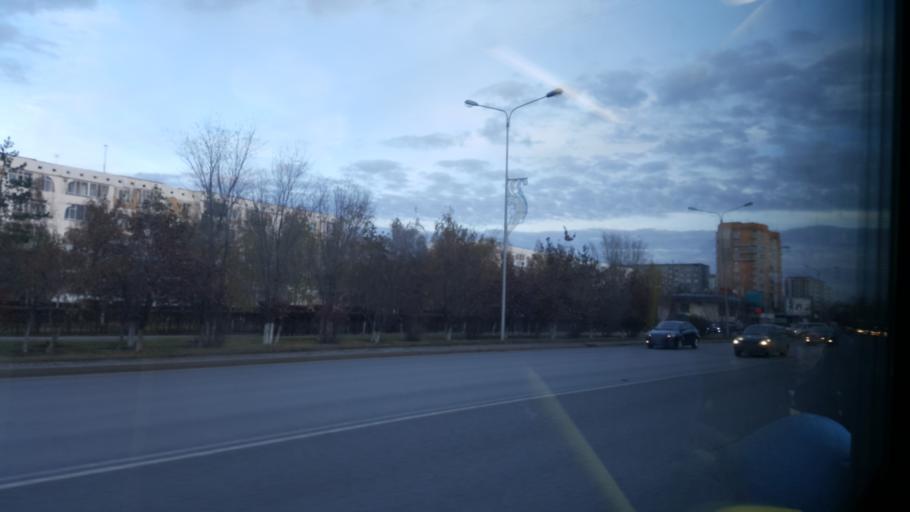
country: KZ
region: Astana Qalasy
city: Astana
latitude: 51.1558
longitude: 71.4823
